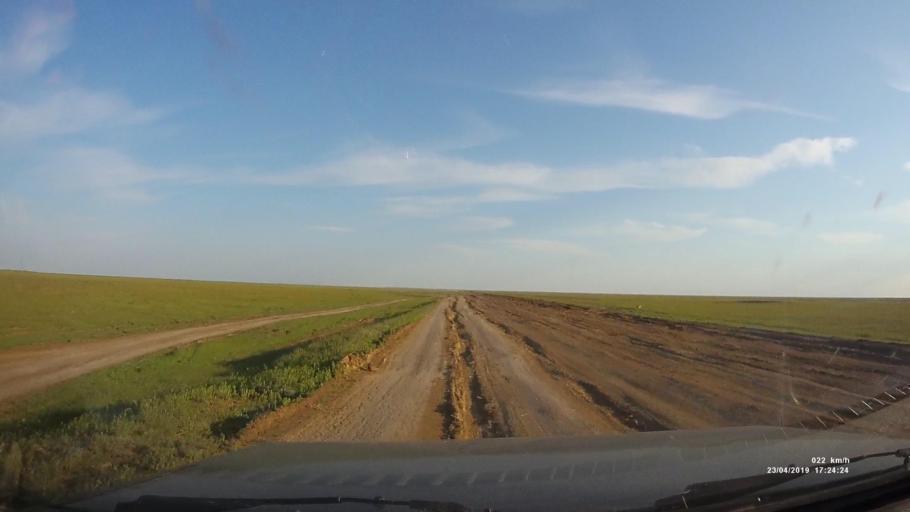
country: RU
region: Kalmykiya
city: Priyutnoye
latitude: 46.1573
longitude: 43.5085
